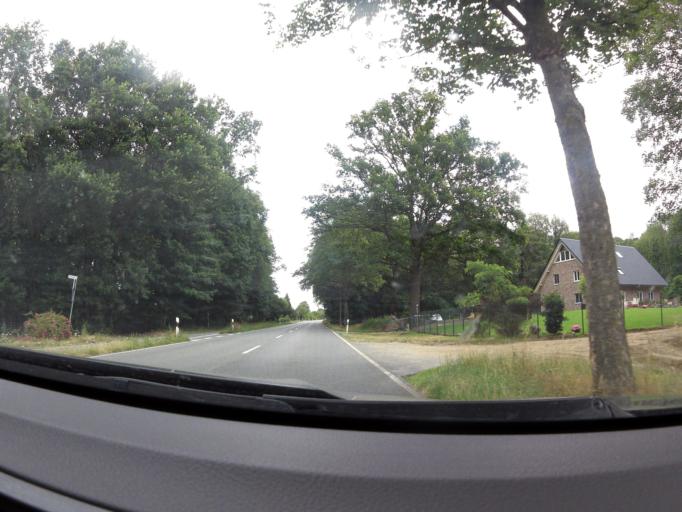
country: DE
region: North Rhine-Westphalia
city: Straelen
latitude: 51.4272
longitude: 6.2457
